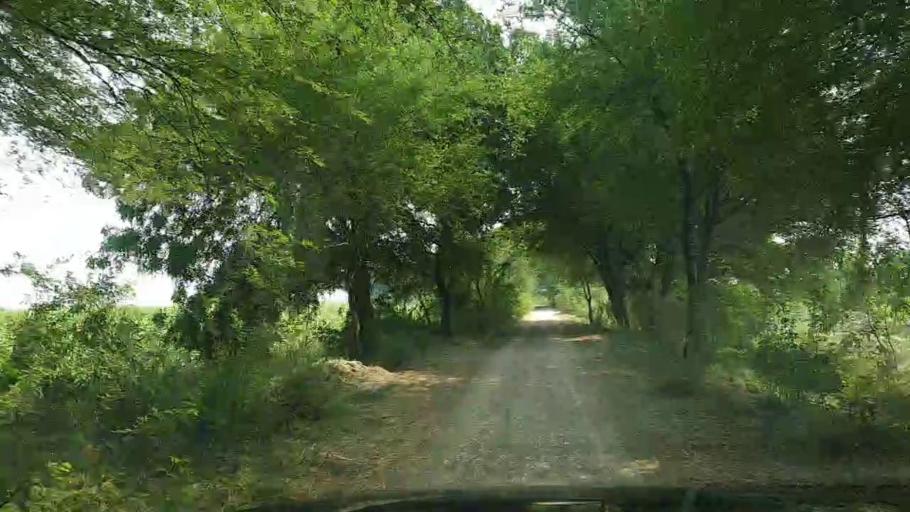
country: PK
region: Sindh
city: Mirpur Batoro
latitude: 24.6898
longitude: 68.2212
